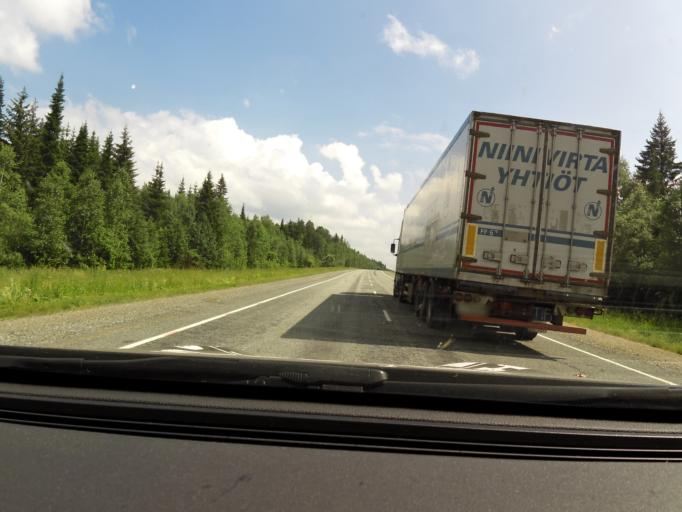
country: RU
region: Sverdlovsk
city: Achit
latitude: 56.8307
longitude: 57.7858
